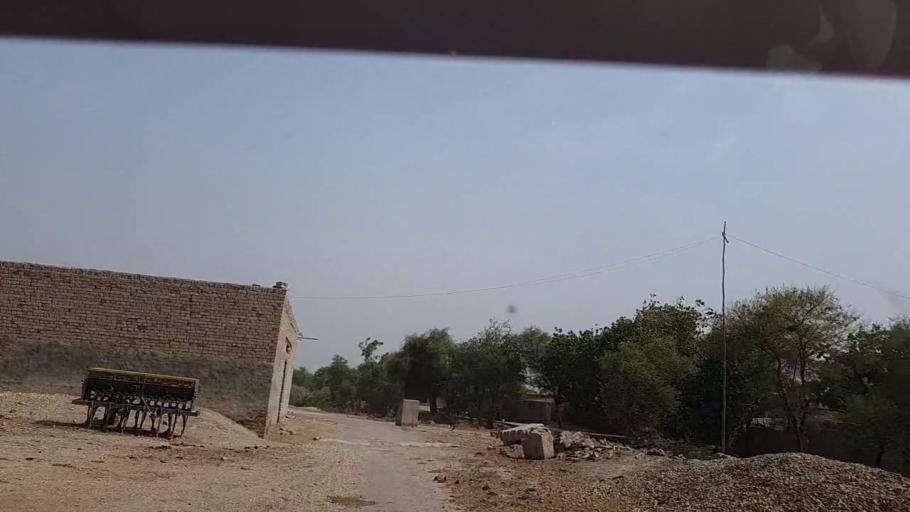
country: PK
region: Sindh
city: Khairpur Nathan Shah
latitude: 27.0321
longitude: 67.6729
